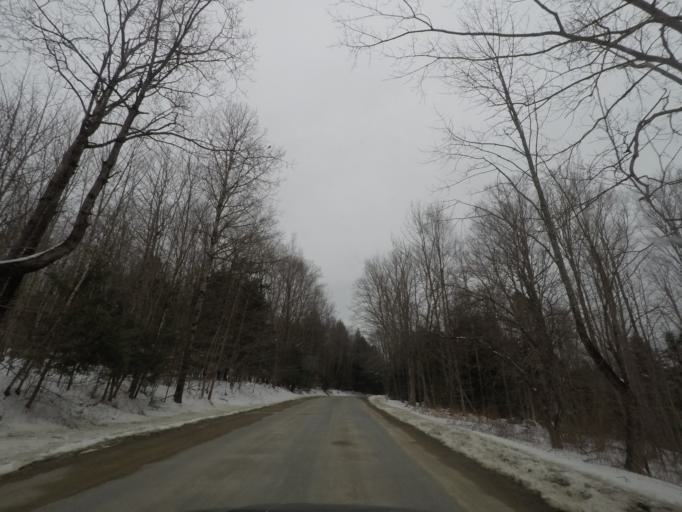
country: US
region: New York
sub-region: Rensselaer County
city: Averill Park
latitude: 42.5620
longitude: -73.4141
